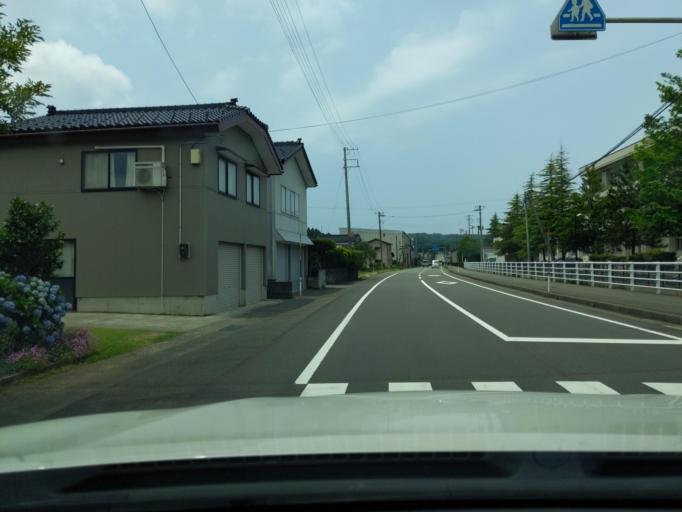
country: JP
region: Niigata
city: Kashiwazaki
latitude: 37.3307
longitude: 138.5665
